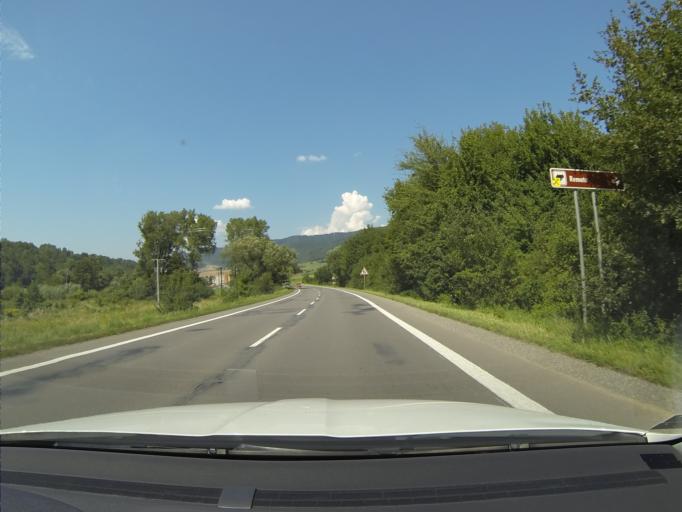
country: SK
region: Nitriansky
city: Handlova
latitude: 48.7566
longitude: 18.7641
